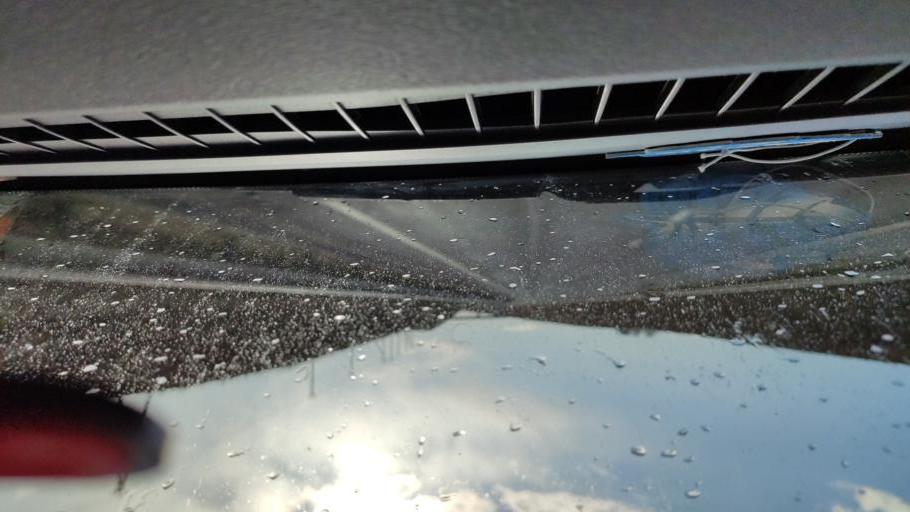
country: RU
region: Saratov
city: Yelshanka
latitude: 51.8201
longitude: 46.3656
